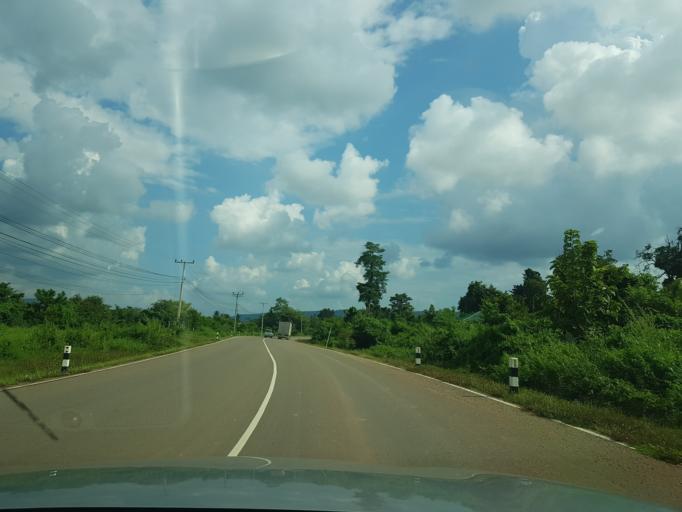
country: TH
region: Nong Khai
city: Sangkhom
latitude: 18.0865
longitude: 102.2914
